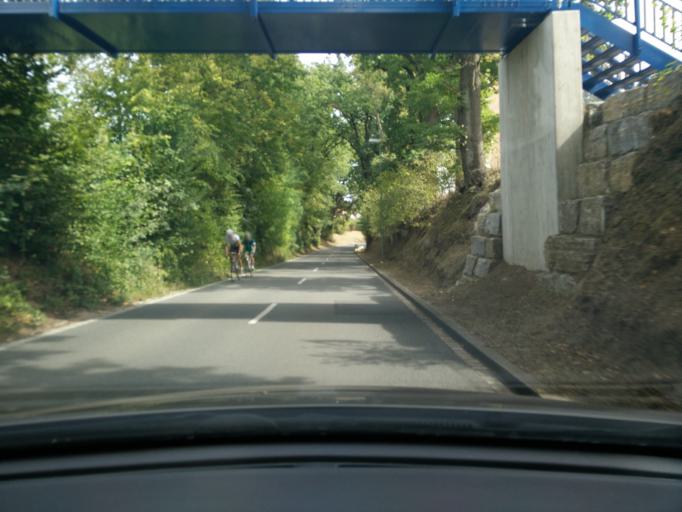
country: DE
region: Bavaria
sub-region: Regierungsbezirk Mittelfranken
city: Veitsbronn
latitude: 49.5125
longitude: 10.8795
